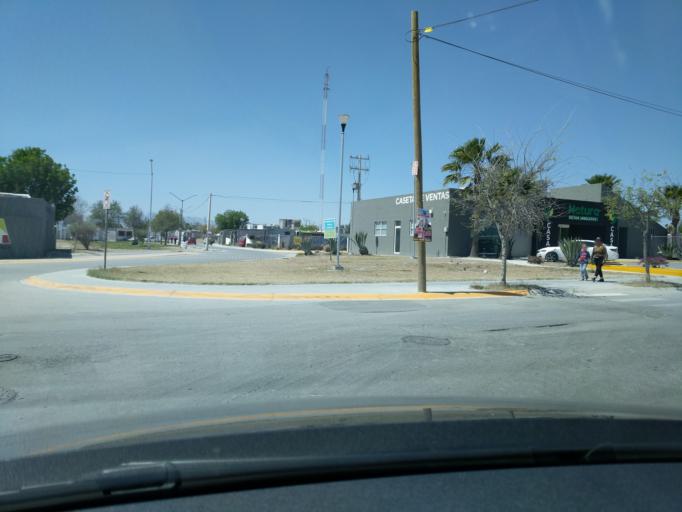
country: MX
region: Nuevo Leon
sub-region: Apodaca
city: Artemio Trevino
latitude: 25.8390
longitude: -100.1376
